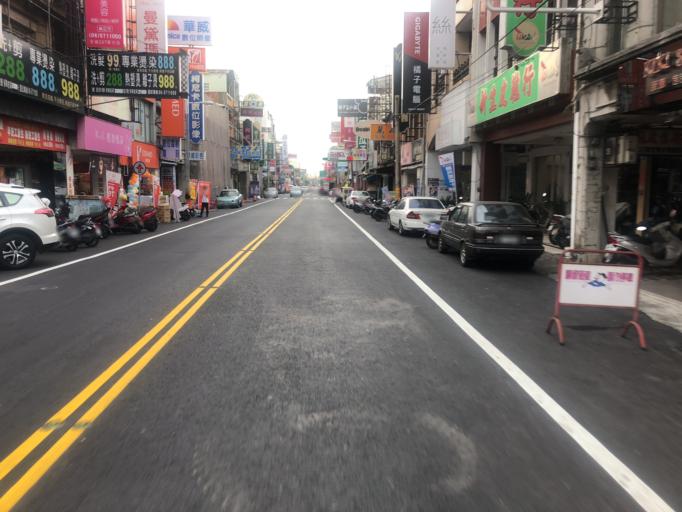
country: TW
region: Taiwan
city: Xinying
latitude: 23.1837
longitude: 120.2508
